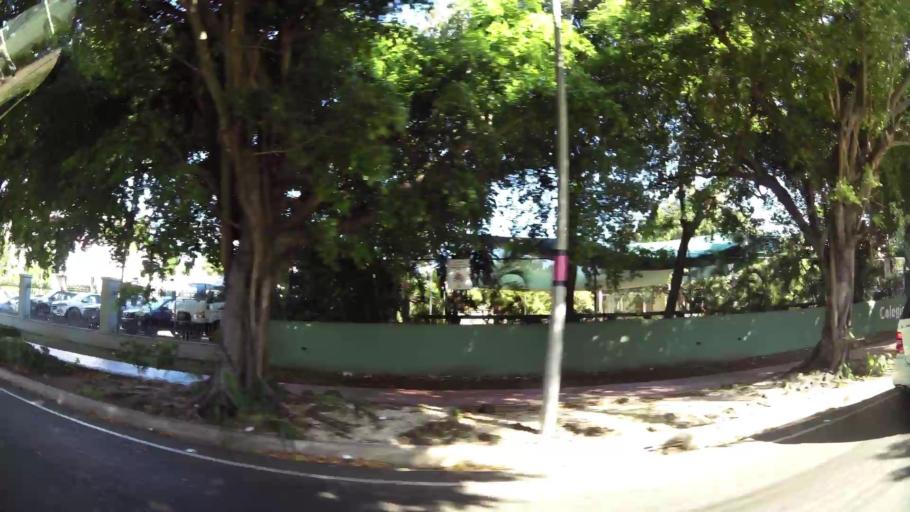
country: DO
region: Nacional
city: Ciudad Nueva
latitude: 18.4631
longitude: -69.9030
